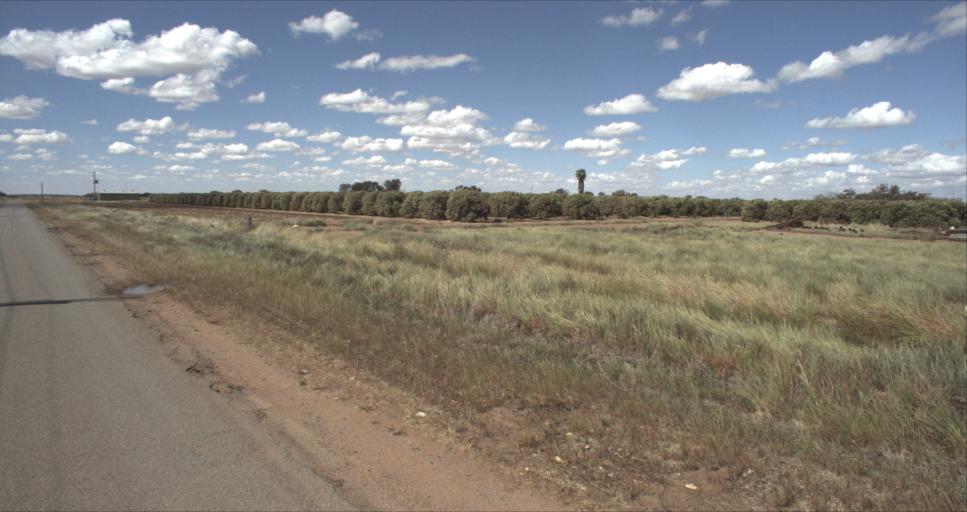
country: AU
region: New South Wales
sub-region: Leeton
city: Leeton
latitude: -34.5106
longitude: 146.2535
